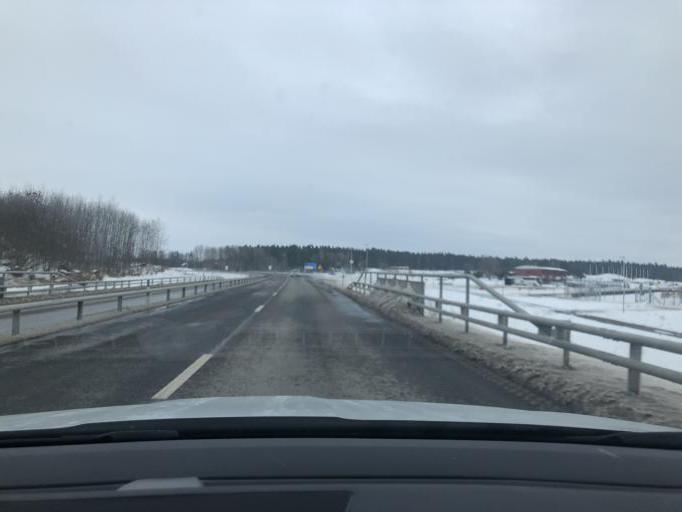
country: SE
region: OEstergoetland
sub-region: Linkopings Kommun
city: Sturefors
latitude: 58.3971
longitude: 15.7163
